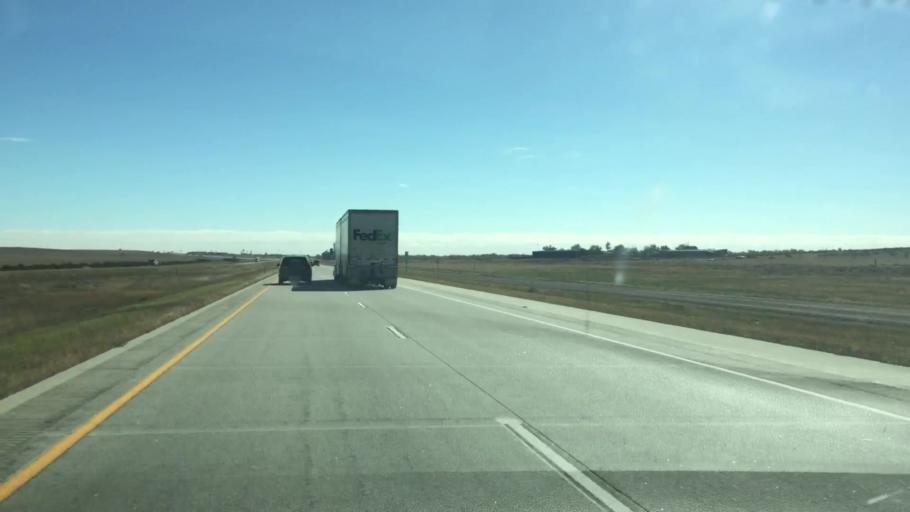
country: US
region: Colorado
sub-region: Lincoln County
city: Limon
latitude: 39.2772
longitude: -103.7534
